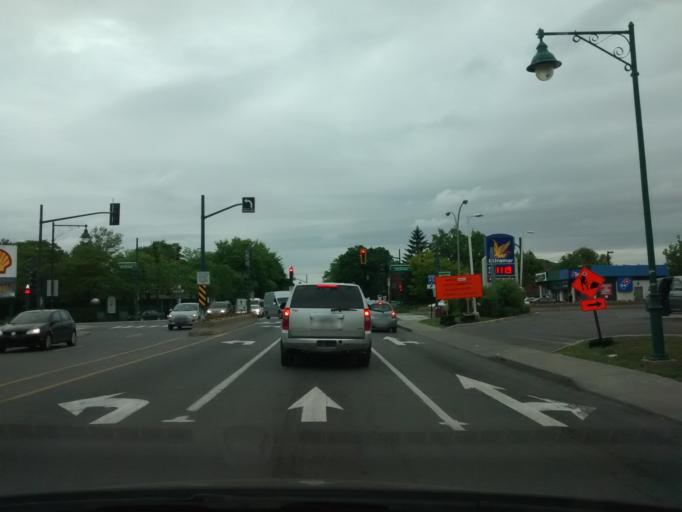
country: CA
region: Quebec
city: Mont-Royal
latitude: 45.5201
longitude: -73.6283
